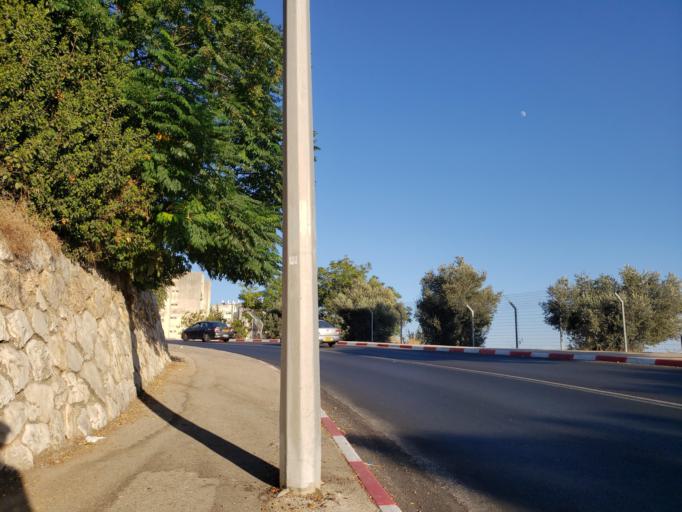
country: IL
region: Northern District
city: Safed
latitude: 32.9573
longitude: 35.4918
